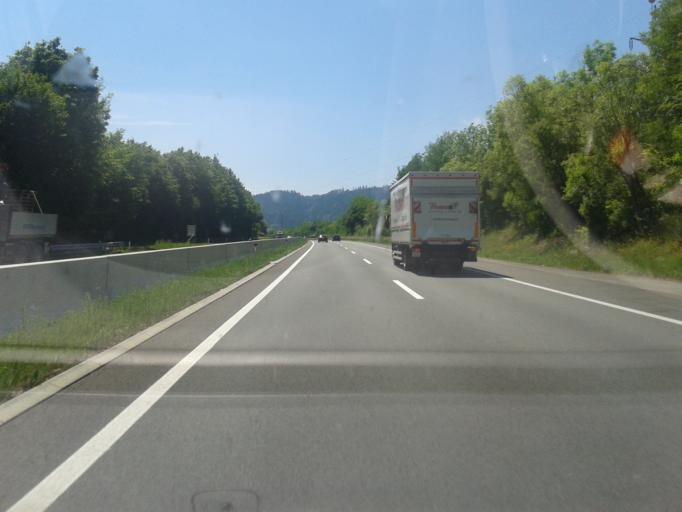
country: AT
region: Carinthia
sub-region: Politischer Bezirk Wolfsberg
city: Sankt Andrae
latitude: 46.7855
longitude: 14.8123
